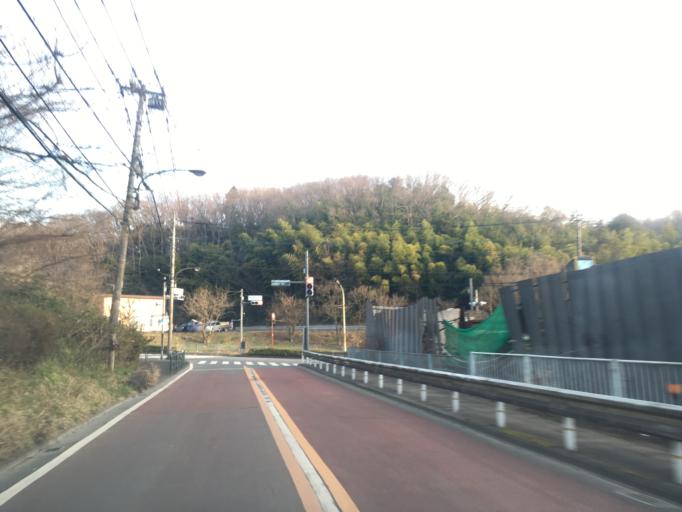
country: JP
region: Tokyo
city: Hino
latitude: 35.6433
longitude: 139.3952
